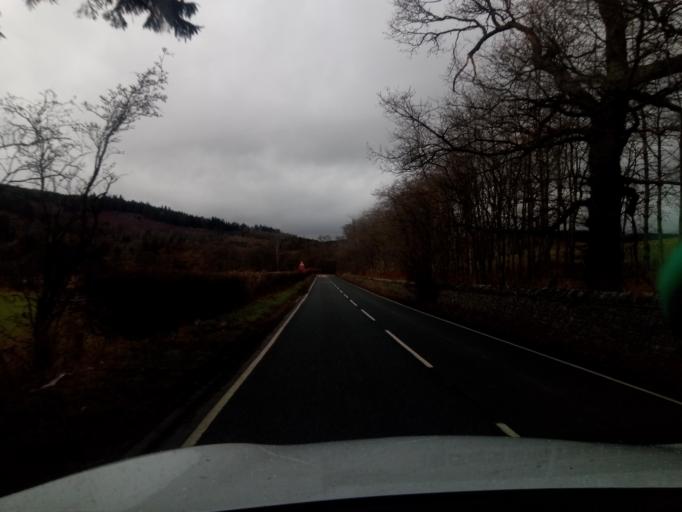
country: GB
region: Scotland
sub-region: The Scottish Borders
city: Innerleithen
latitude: 55.6290
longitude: -3.0963
